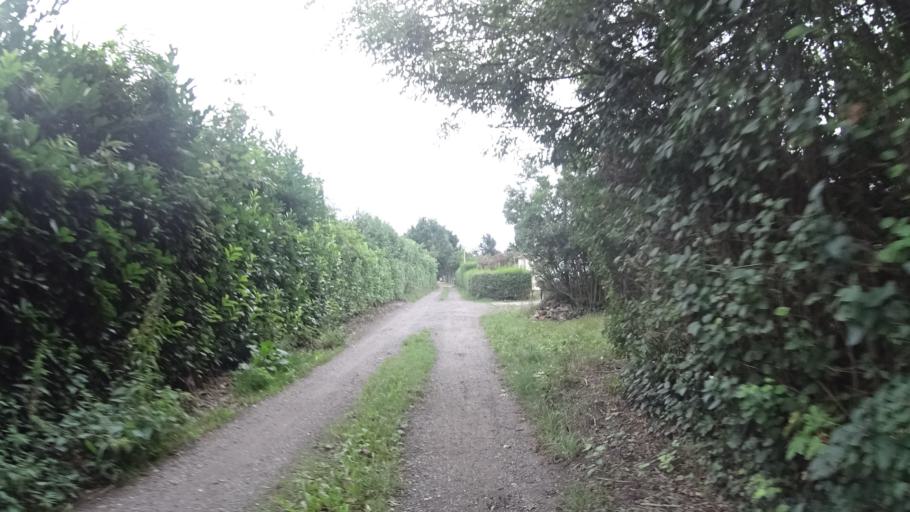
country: NL
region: Groningen
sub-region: Gemeente Slochteren
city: Slochteren
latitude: 53.2248
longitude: 6.8032
